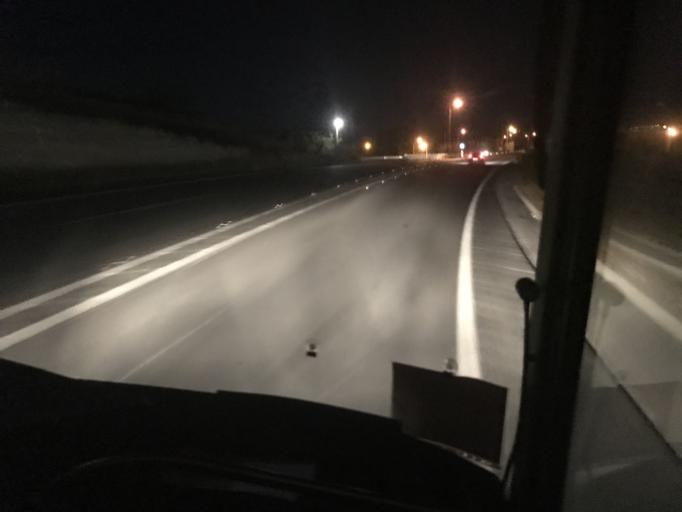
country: GR
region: Crete
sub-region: Nomos Irakleiou
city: Skalanion
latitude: 35.2631
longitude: 25.1819
